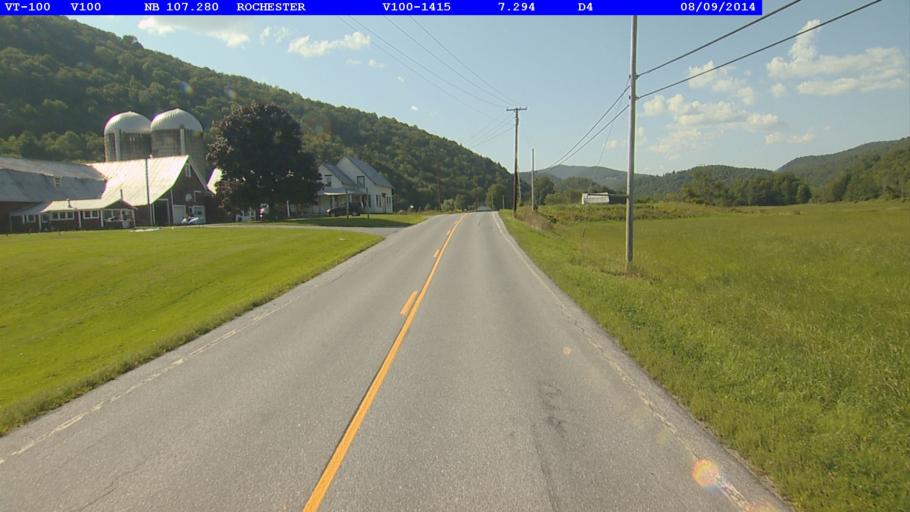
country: US
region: Vermont
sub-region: Orange County
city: Randolph
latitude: 43.8990
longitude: -72.8230
